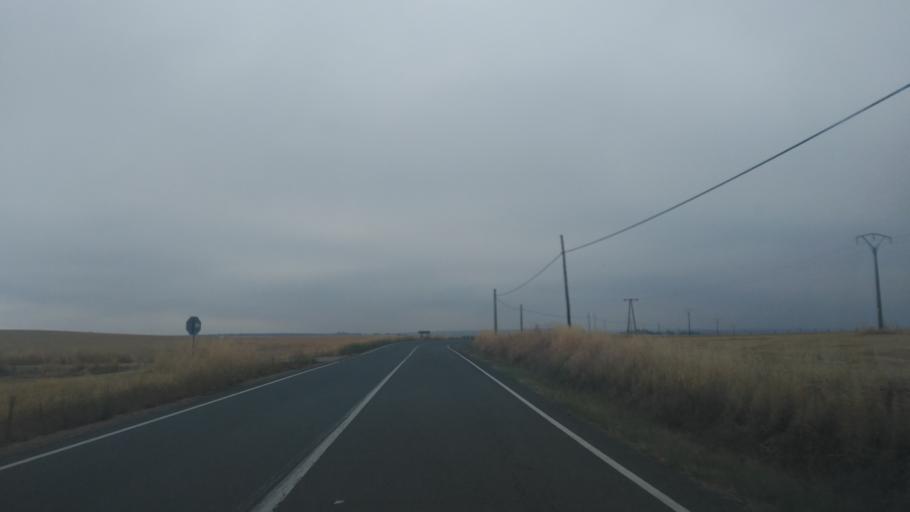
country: ES
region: Castille and Leon
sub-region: Provincia de Salamanca
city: Matilla de los Canos del Rio
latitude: 40.8411
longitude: -5.9499
